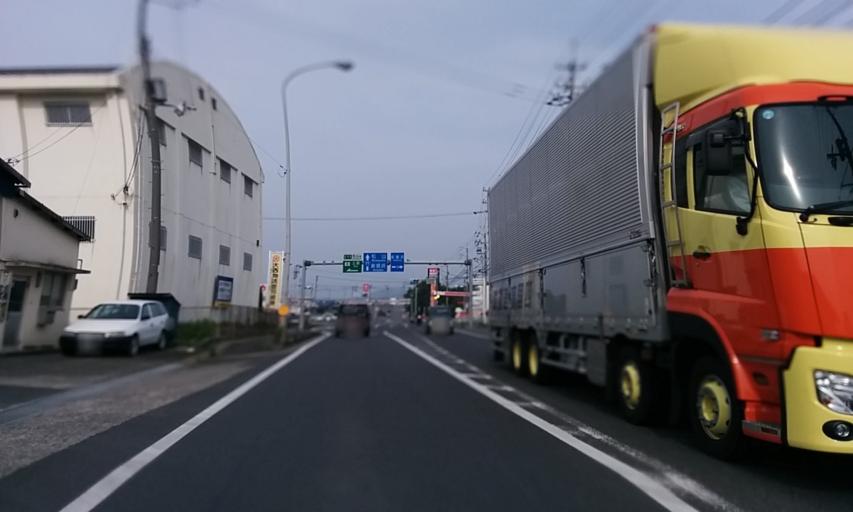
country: JP
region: Ehime
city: Kawanoecho
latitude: 33.9651
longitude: 133.4699
